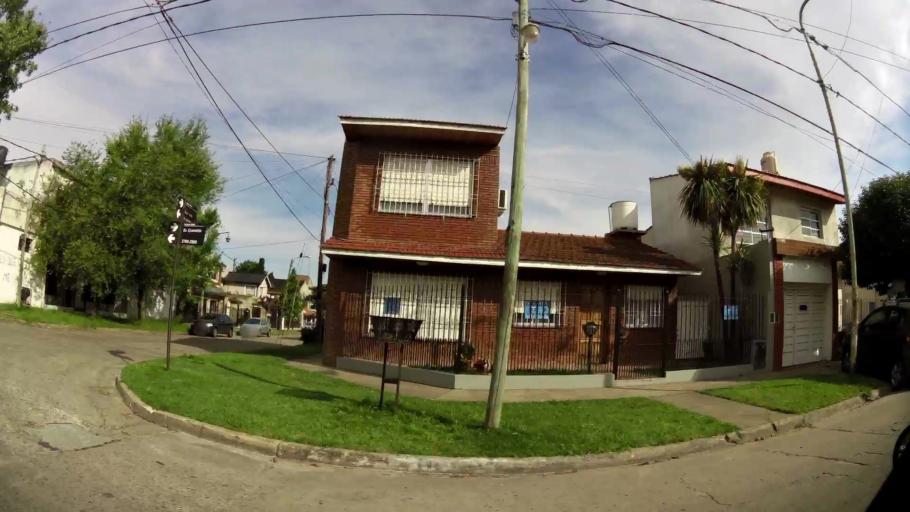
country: AR
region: Buenos Aires
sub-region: Partido de Quilmes
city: Quilmes
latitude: -34.7591
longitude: -58.2735
